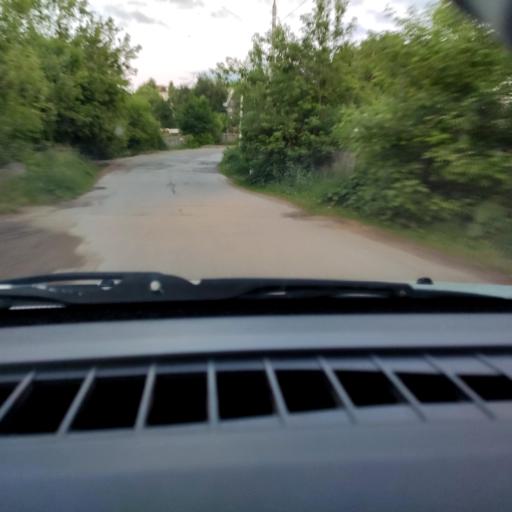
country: RU
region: Perm
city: Perm
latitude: 58.1168
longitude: 56.3109
